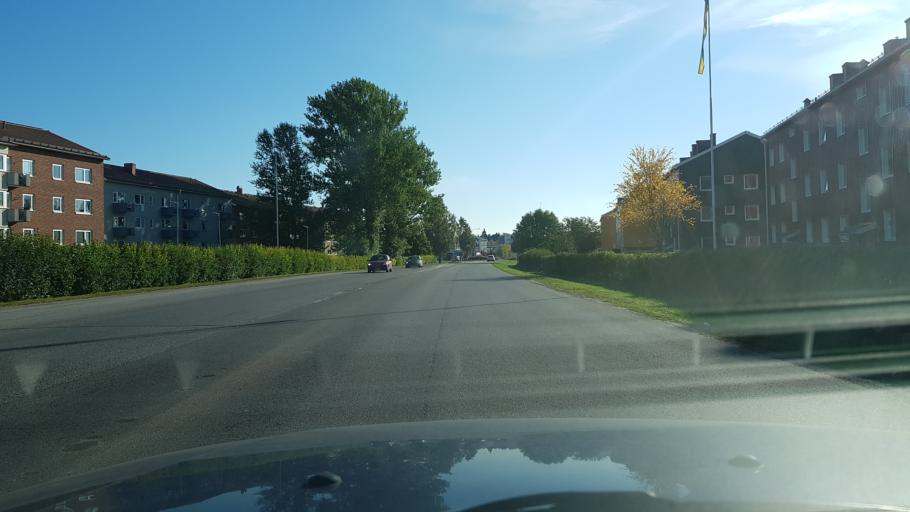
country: SE
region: Norrbotten
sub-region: Pitea Kommun
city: Pitea
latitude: 65.3219
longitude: 21.4681
